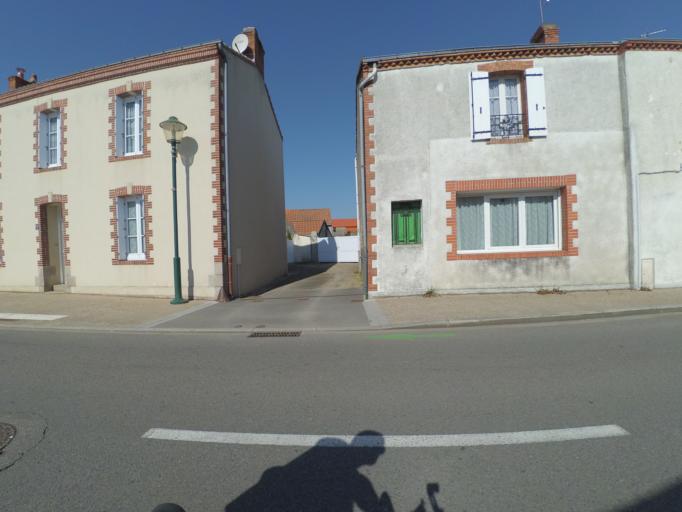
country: FR
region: Pays de la Loire
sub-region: Departement de la Loire-Atlantique
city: Chemere
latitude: 47.1220
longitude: -1.9158
